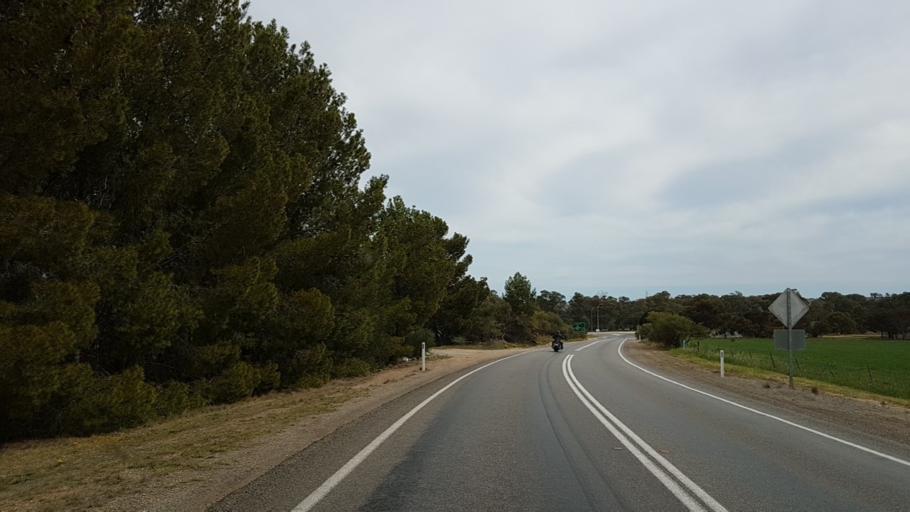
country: AU
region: South Australia
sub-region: Port Pirie City and Dists
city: Crystal Brook
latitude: -33.2639
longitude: 138.3493
